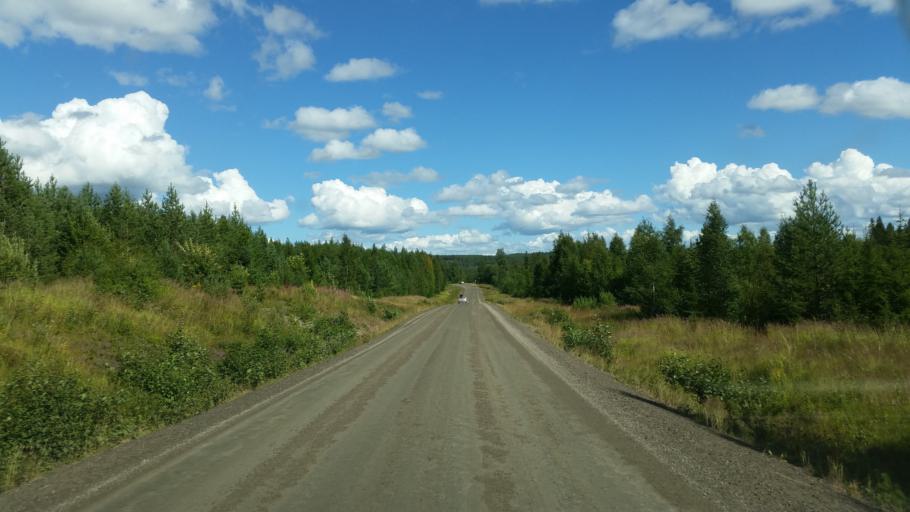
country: SE
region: Gaevleborg
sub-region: Ljusdals Kommun
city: Ljusdal
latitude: 61.9246
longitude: 16.1485
